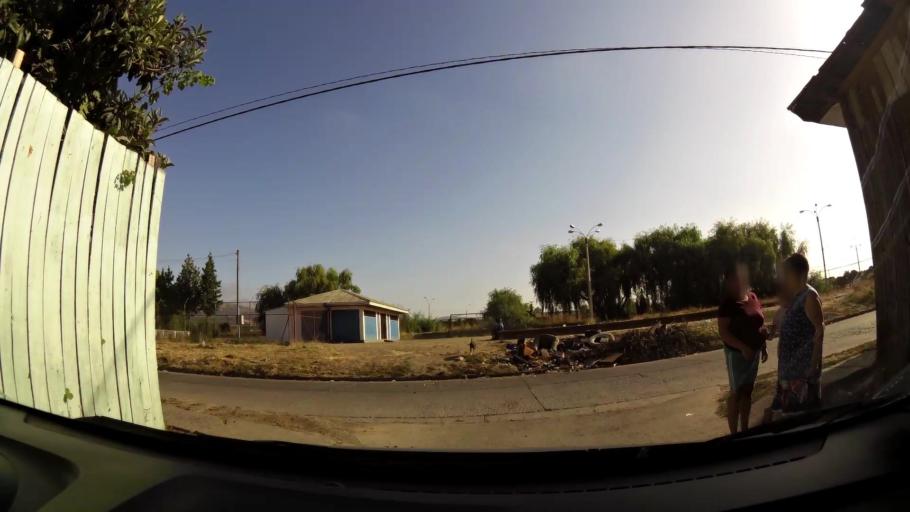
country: CL
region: Maule
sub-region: Provincia de Talca
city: Talca
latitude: -35.4042
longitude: -71.6540
